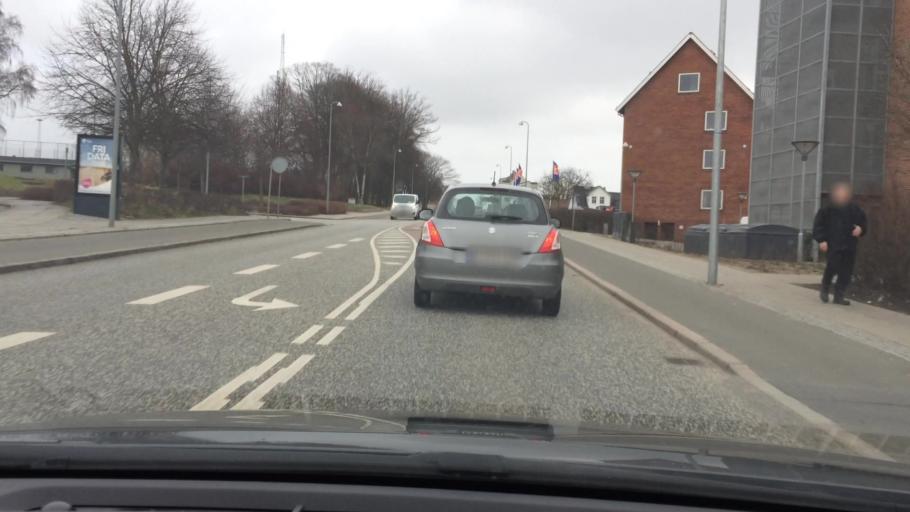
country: DK
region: Central Jutland
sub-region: Horsens Kommune
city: Horsens
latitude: 55.8717
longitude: 9.8319
